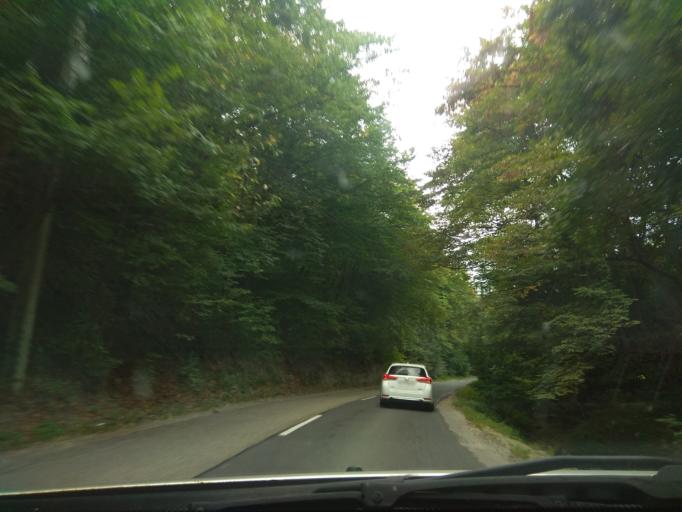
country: HU
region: Borsod-Abauj-Zemplen
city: Miskolc
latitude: 48.0812
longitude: 20.6993
